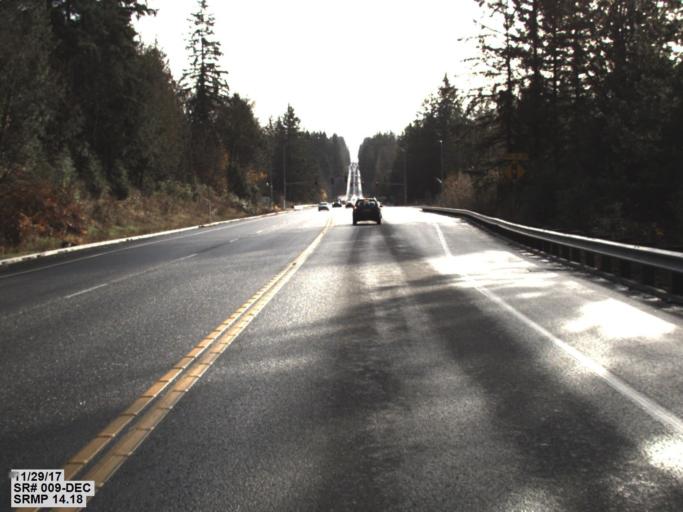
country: US
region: Washington
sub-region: Snohomish County
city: West Lake Stevens
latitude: 47.9802
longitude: -122.1028
